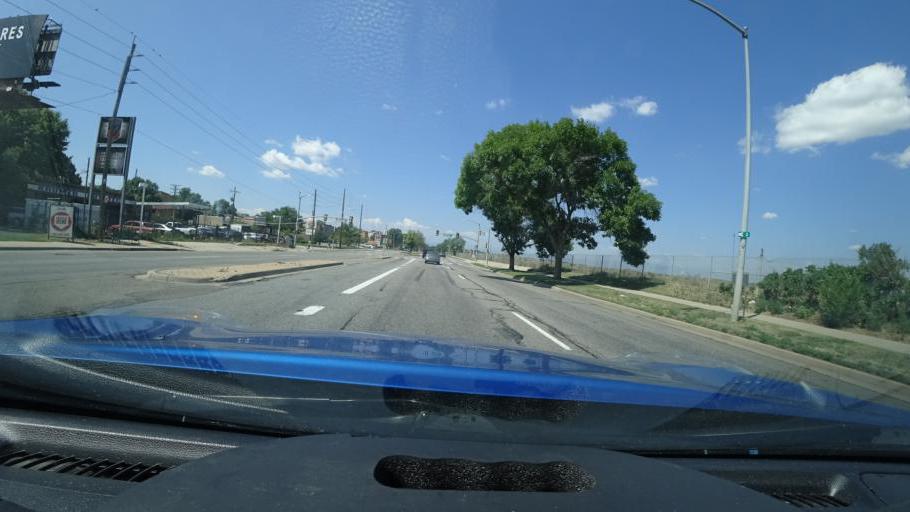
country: US
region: Colorado
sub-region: Adams County
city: Aurora
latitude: 39.7092
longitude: -104.8746
